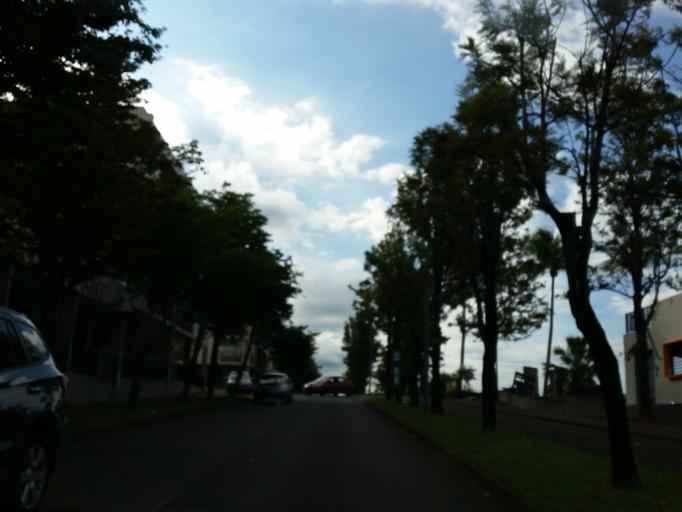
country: RE
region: Reunion
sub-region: Reunion
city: Sainte-Marie
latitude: -20.9070
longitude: 55.5016
